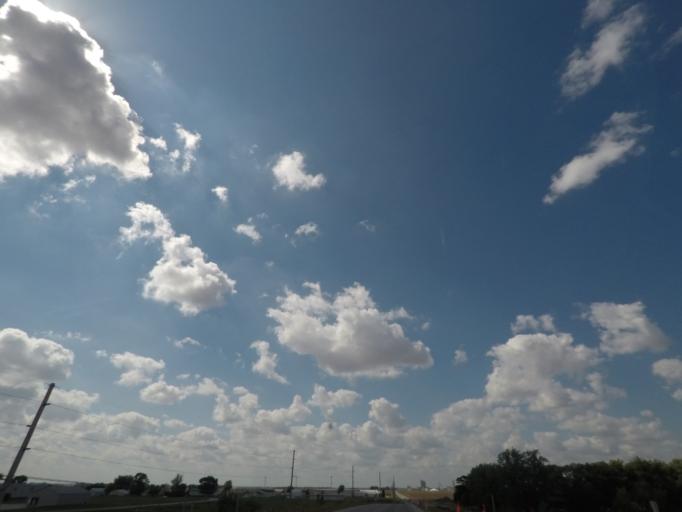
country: US
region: Iowa
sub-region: Story County
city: Nevada
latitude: 42.0228
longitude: -93.4774
